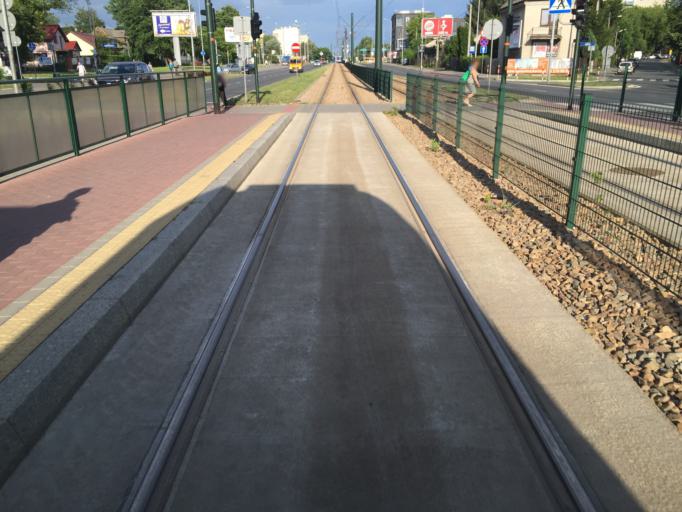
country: PL
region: Lesser Poland Voivodeship
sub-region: Krakow
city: Krakow
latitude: 50.0740
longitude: 20.0116
